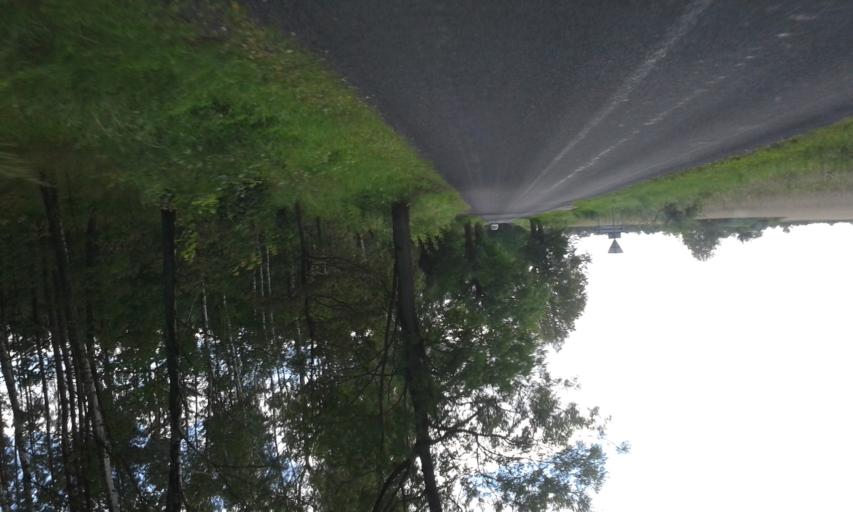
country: PL
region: West Pomeranian Voivodeship
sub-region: Powiat walecki
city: Walcz
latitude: 53.2467
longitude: 16.5387
